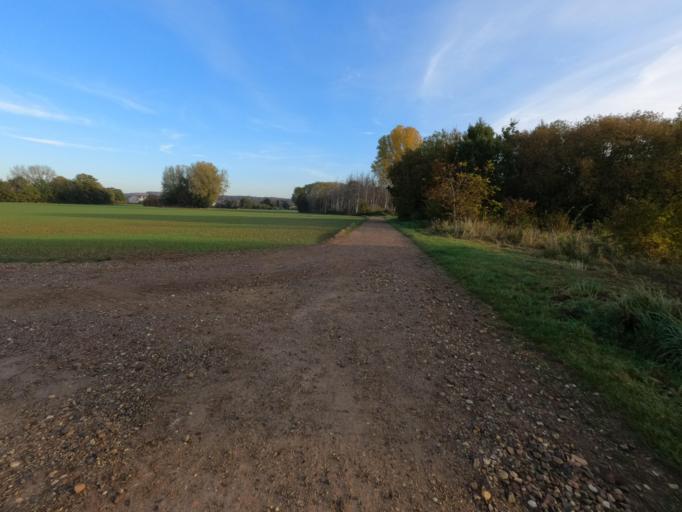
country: DE
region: North Rhine-Westphalia
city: Huckelhoven
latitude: 51.0518
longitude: 6.1967
